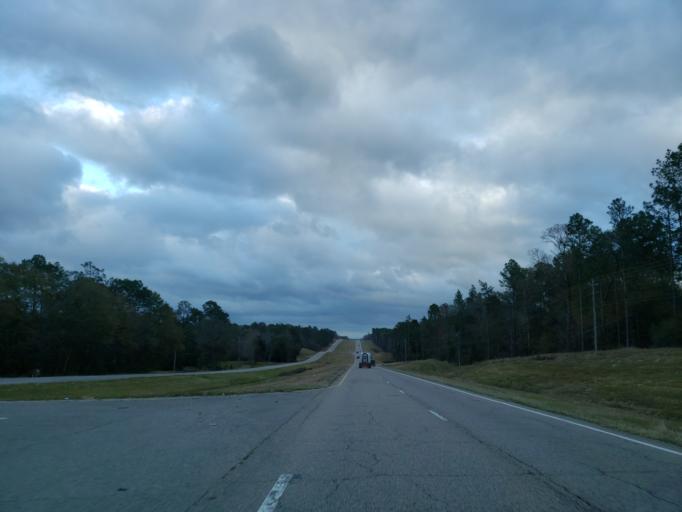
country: US
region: Mississippi
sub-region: George County
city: Lucedale
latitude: 30.9188
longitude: -88.5006
